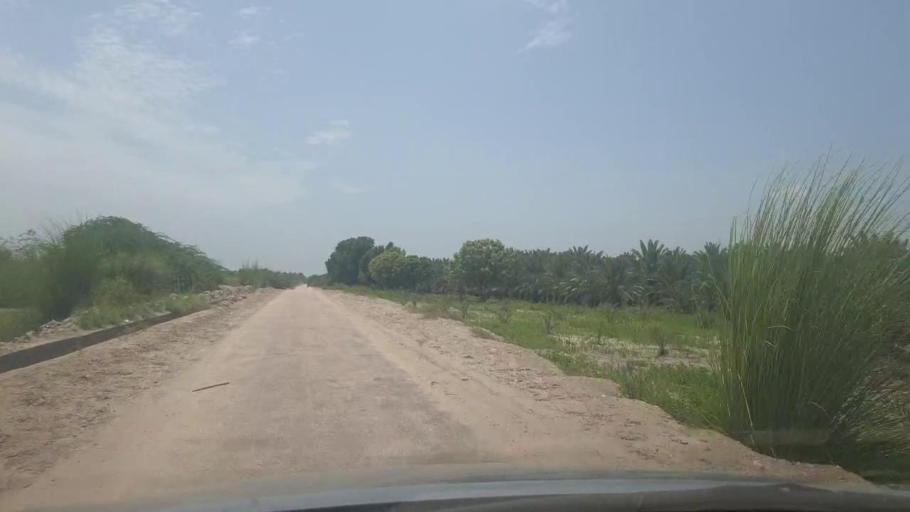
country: PK
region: Sindh
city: Kot Diji
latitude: 27.4062
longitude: 68.7283
